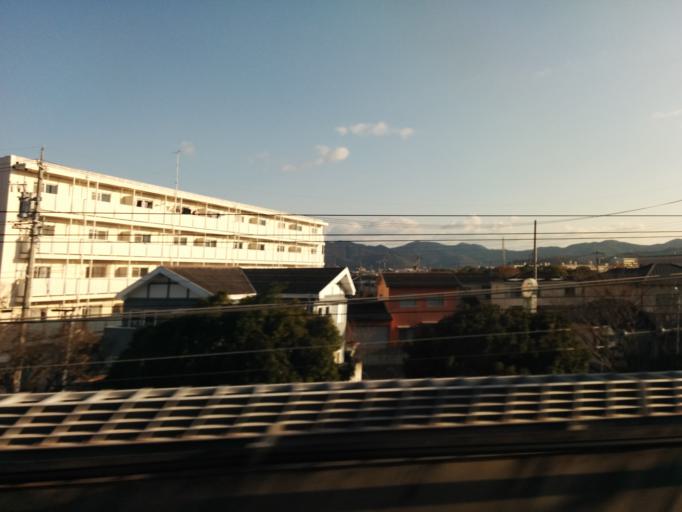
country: JP
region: Aichi
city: Toyohashi
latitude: 34.7380
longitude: 137.4062
